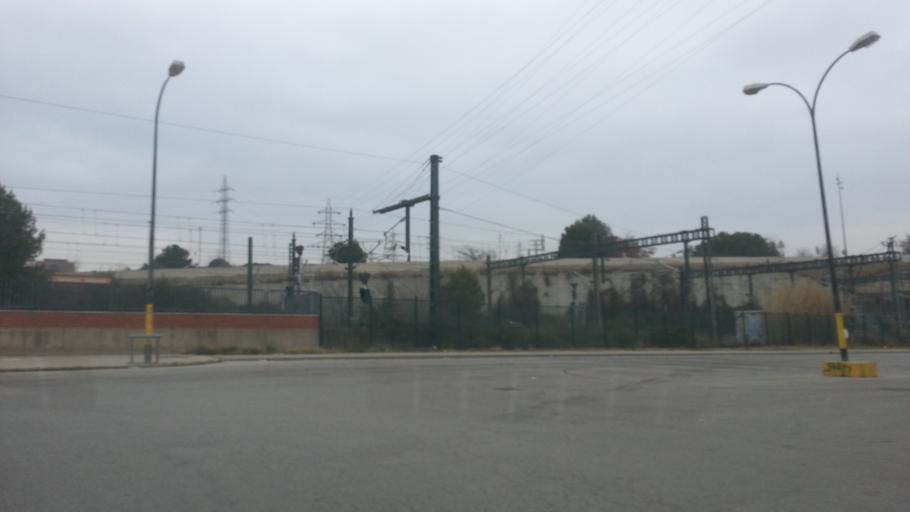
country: ES
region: Catalonia
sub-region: Provincia de Barcelona
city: Barbera del Valles
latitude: 41.4975
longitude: 2.1159
